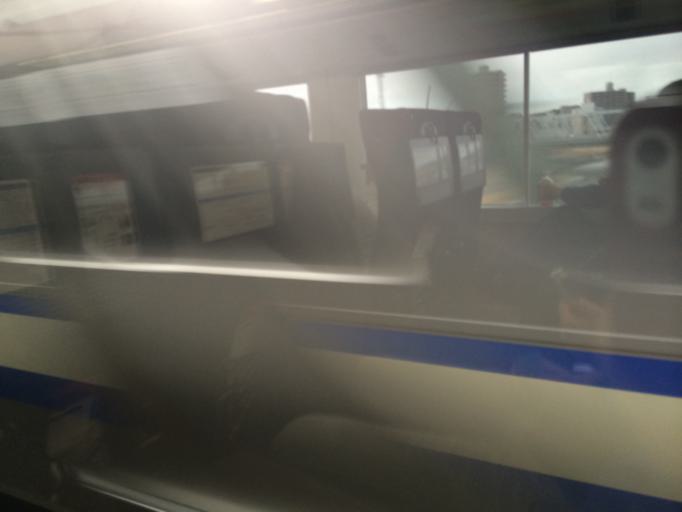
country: JP
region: Chiba
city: Matsudo
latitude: 35.7326
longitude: 139.8991
